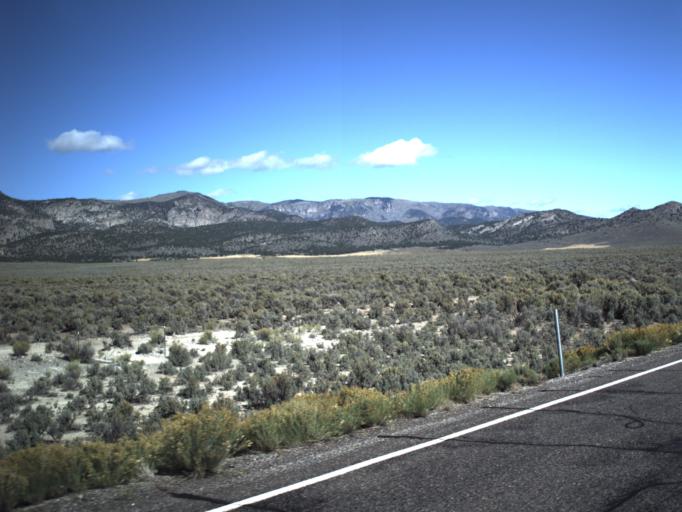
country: US
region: Utah
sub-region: Piute County
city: Junction
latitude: 38.2731
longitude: -111.9859
